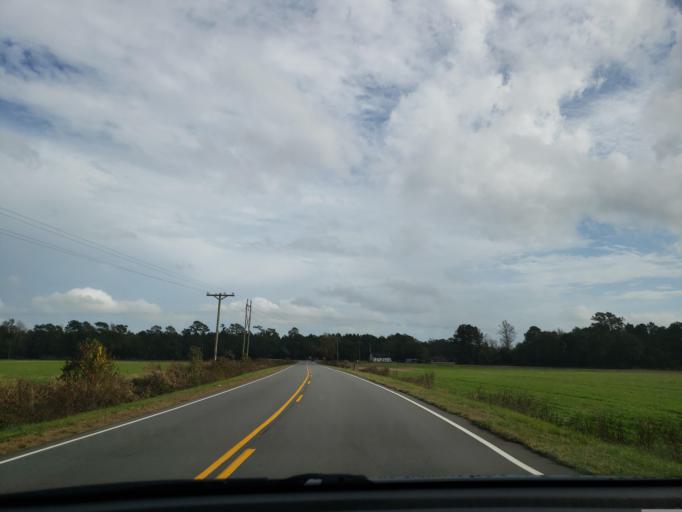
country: US
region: North Carolina
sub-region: Duplin County
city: Beulaville
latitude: 34.8254
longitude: -77.8430
